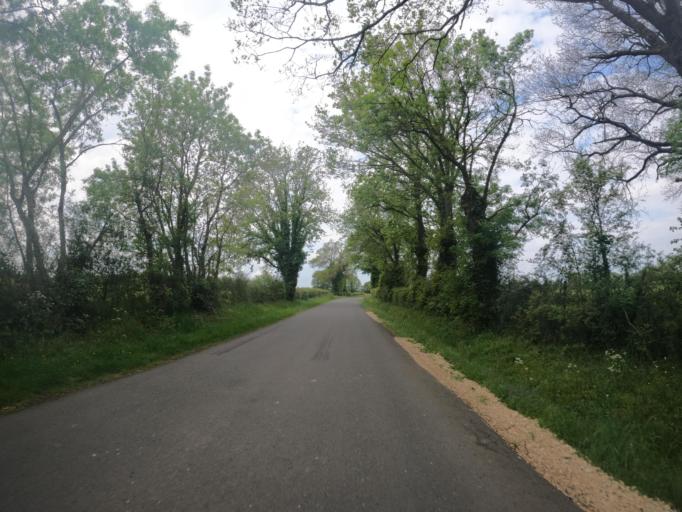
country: FR
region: Poitou-Charentes
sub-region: Departement des Deux-Sevres
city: Saint-Varent
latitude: 46.8677
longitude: -0.2819
